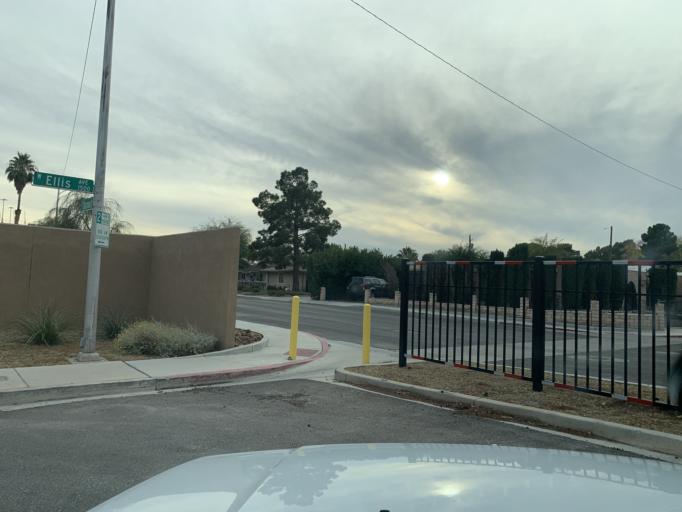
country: US
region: Nevada
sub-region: Clark County
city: Las Vegas
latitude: 36.1571
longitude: -115.1622
